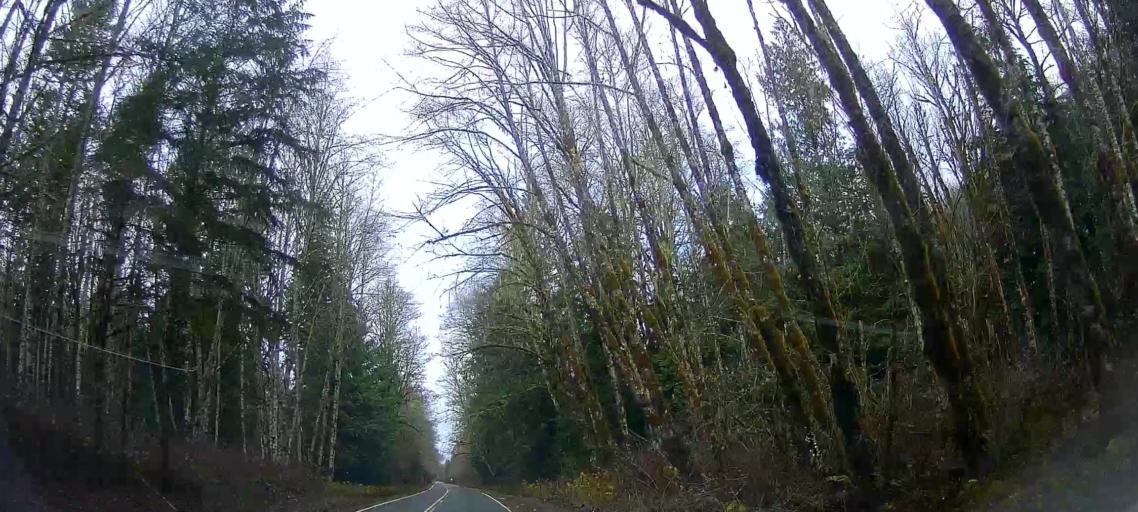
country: US
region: Washington
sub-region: Snohomish County
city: Darrington
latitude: 48.5012
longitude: -121.4614
